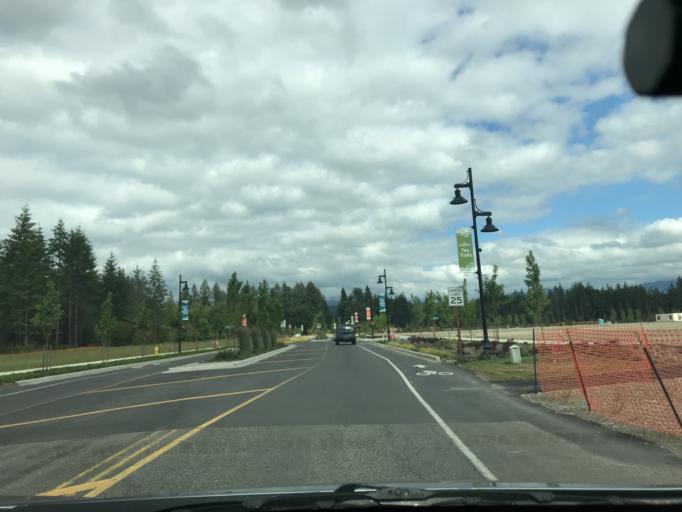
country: US
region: Washington
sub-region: King County
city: Black Diamond
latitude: 47.3112
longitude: -122.0337
